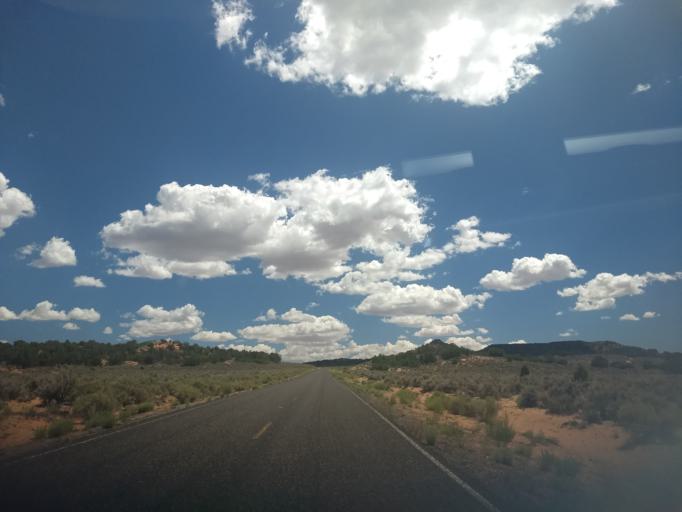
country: US
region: Utah
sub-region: Kane County
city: Kanab
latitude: 37.1437
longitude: -112.6746
